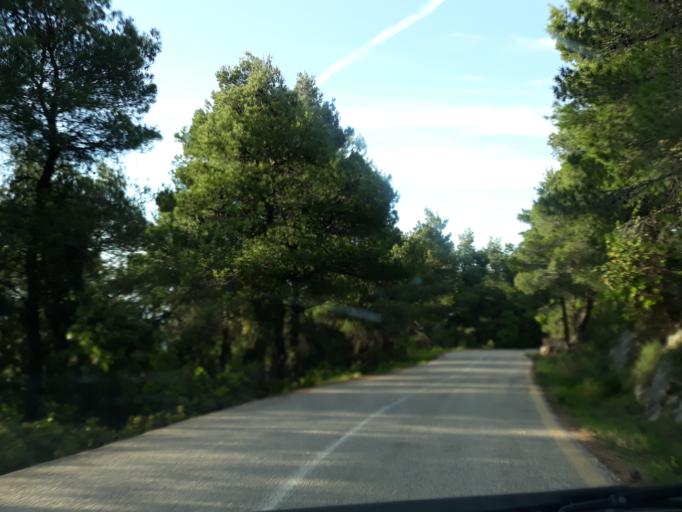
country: GR
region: Attica
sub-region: Nomarchia Anatolikis Attikis
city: Afidnes
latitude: 38.2209
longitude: 23.7804
